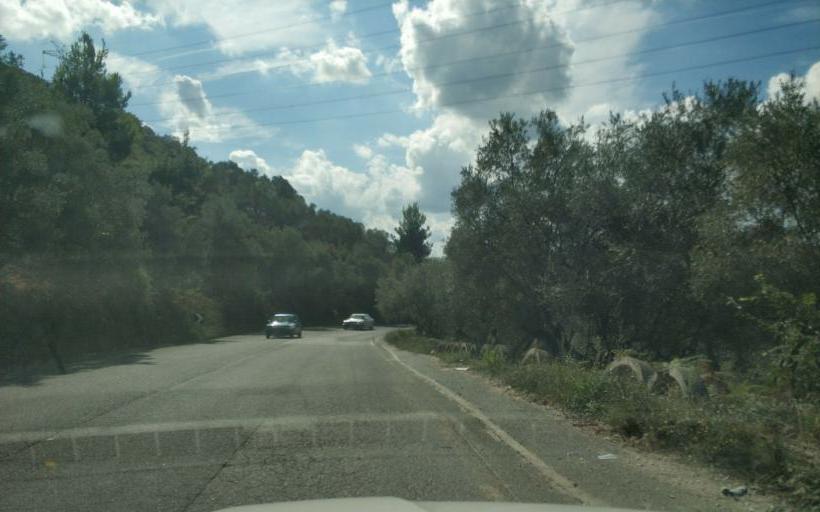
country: AL
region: Durres
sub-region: Rrethi i Krujes
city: Kruje
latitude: 41.4857
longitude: 19.7668
